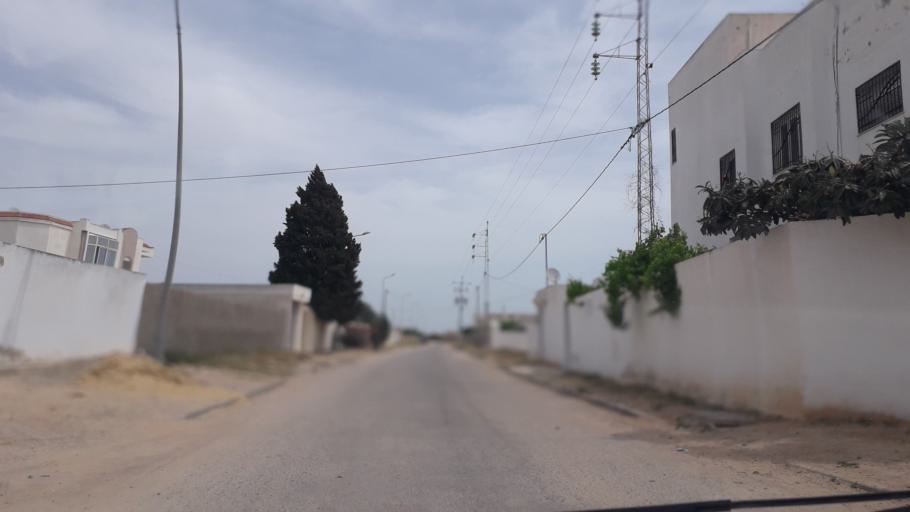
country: TN
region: Safaqis
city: Al Qarmadah
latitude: 34.8084
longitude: 10.7689
